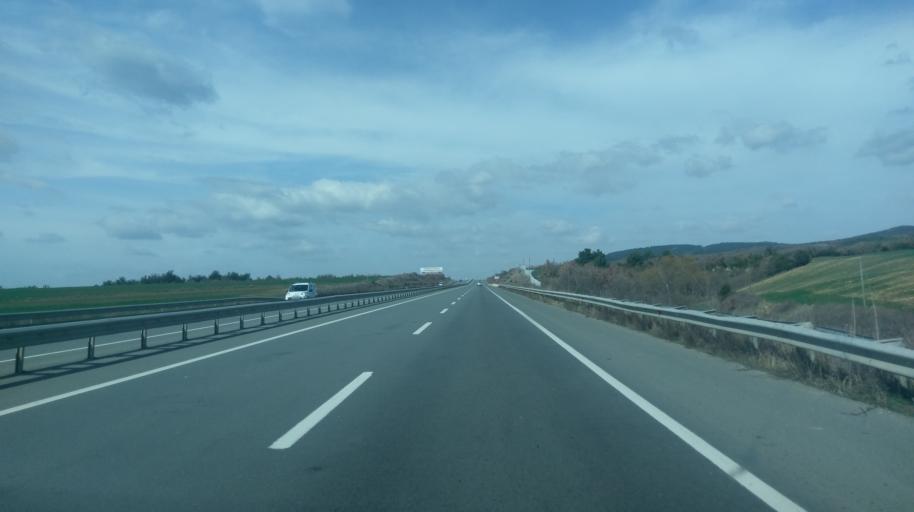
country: TR
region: Edirne
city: Kesan
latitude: 40.7984
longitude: 26.6685
